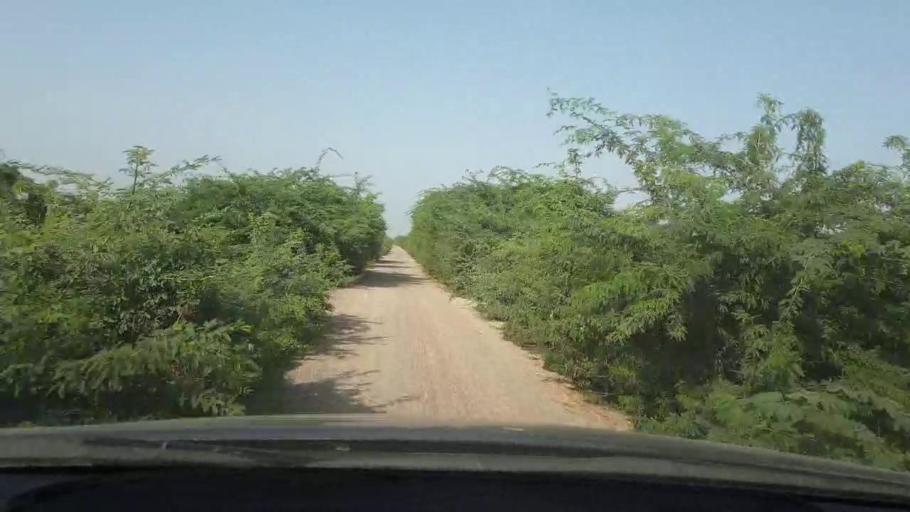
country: PK
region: Sindh
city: Naukot
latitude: 24.7978
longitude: 69.3034
